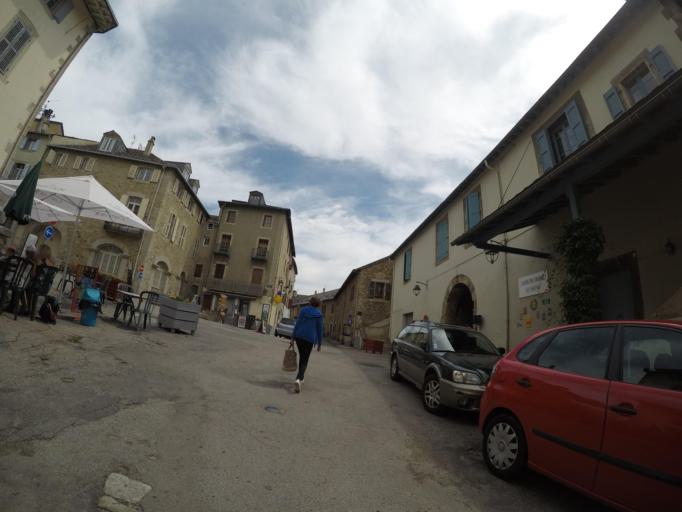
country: ES
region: Catalonia
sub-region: Provincia de Girona
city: Llivia
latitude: 42.5079
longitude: 2.1220
